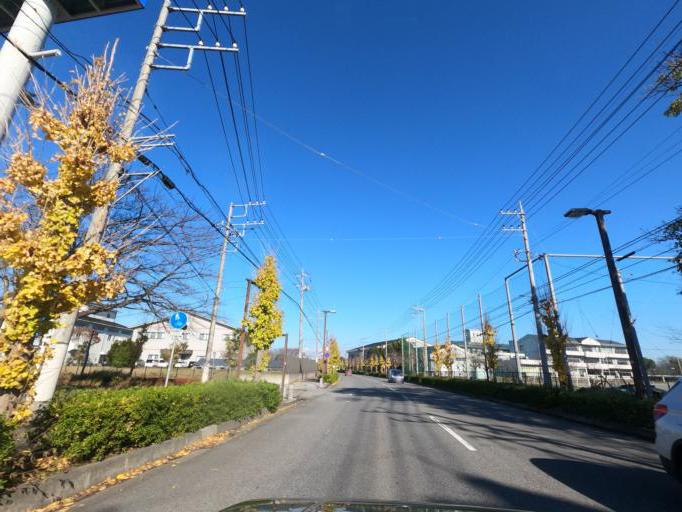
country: JP
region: Ibaraki
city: Mitsukaido
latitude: 35.9797
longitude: 139.9762
